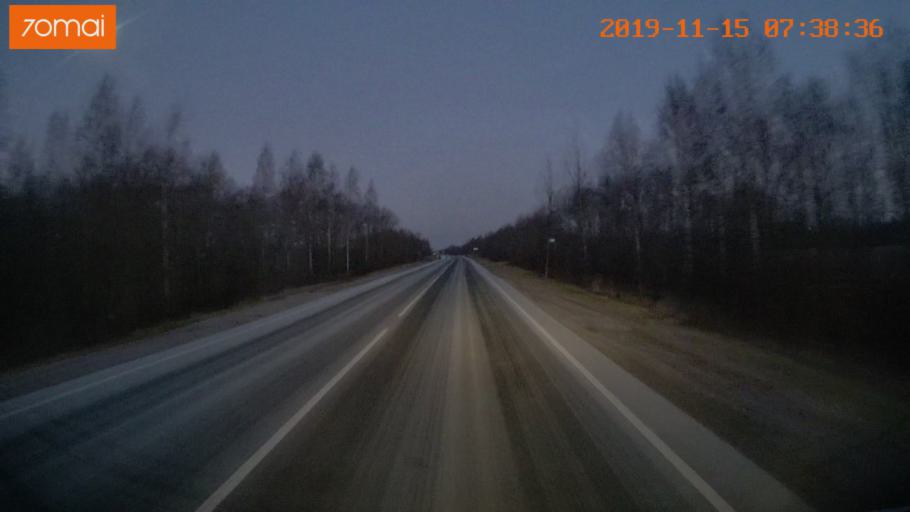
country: RU
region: Vologda
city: Sheksna
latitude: 58.7586
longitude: 38.3981
